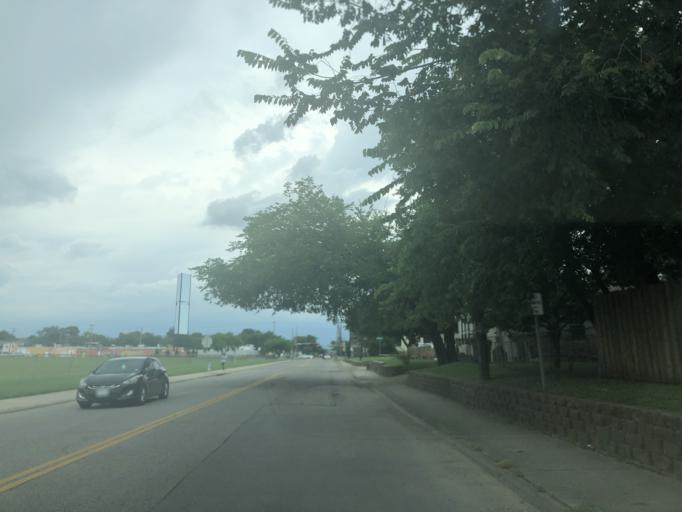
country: US
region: Texas
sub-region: Dallas County
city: Irving
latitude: 32.8062
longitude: -96.9345
